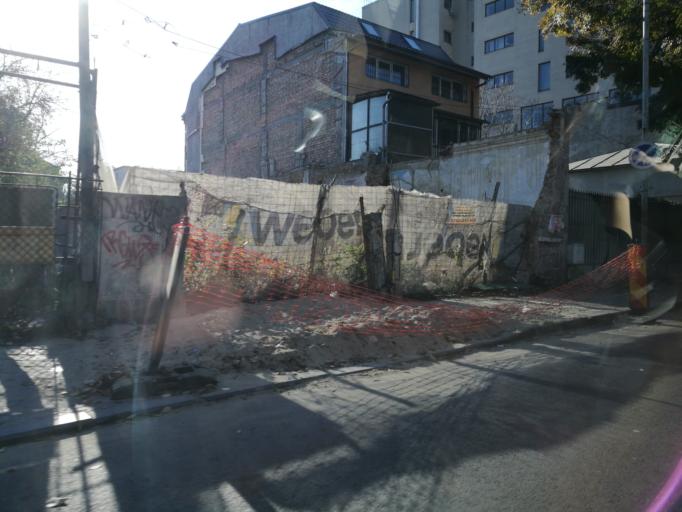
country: RO
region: Bucuresti
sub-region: Municipiul Bucuresti
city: Bucharest
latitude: 44.4465
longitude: 26.1145
